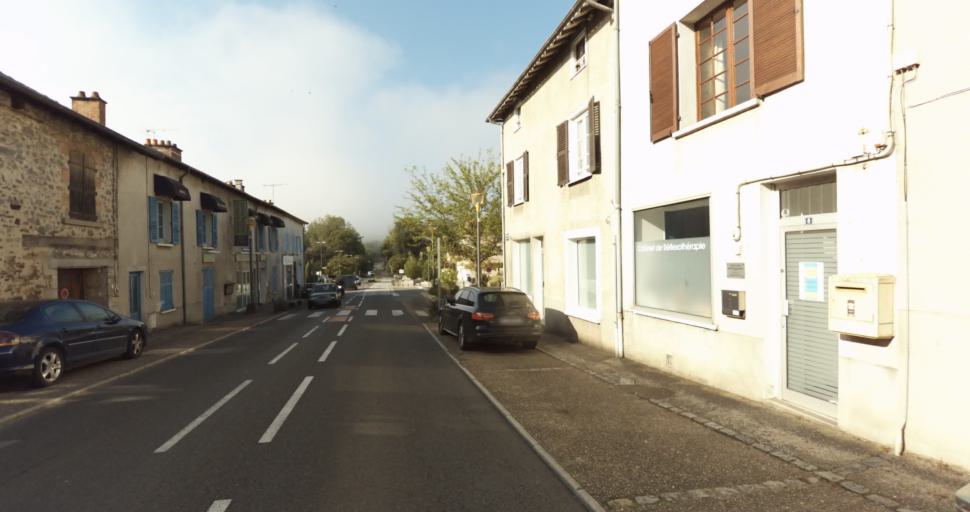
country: FR
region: Limousin
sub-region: Departement de la Haute-Vienne
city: Le Vigen
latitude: 45.7513
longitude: 1.2894
